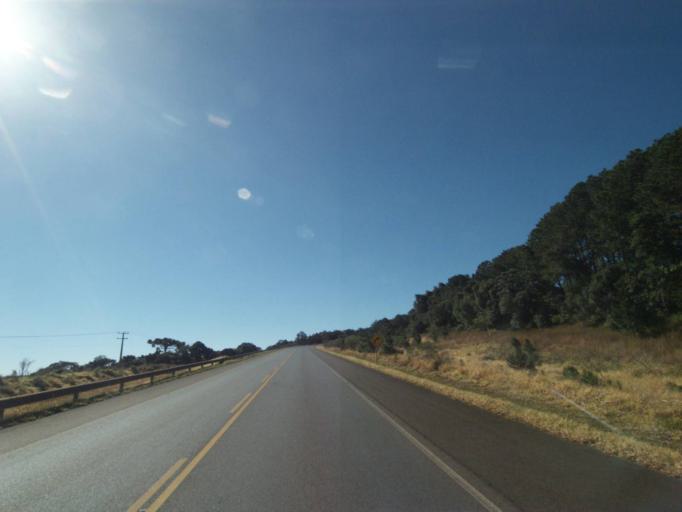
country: BR
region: Parana
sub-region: Tibagi
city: Tibagi
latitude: -24.4131
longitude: -50.3651
